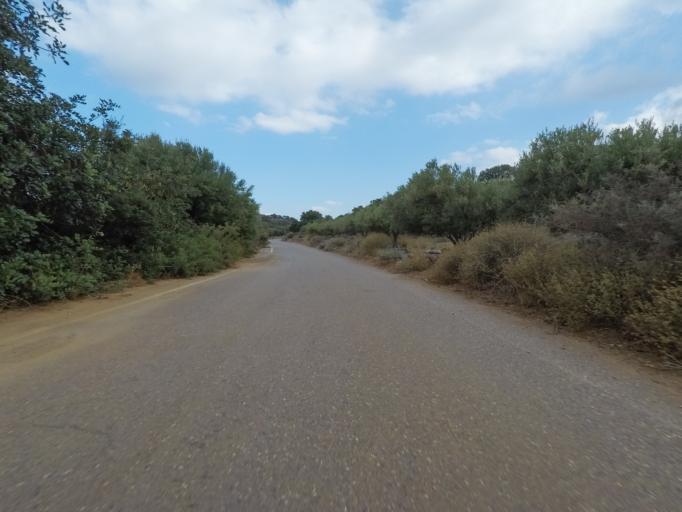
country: GR
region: Crete
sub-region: Nomos Lasithiou
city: Kritsa
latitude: 35.1706
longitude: 25.6537
